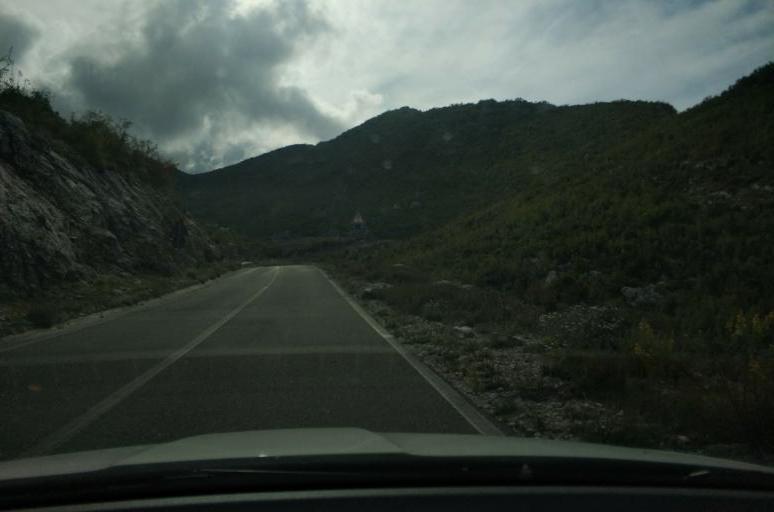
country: AL
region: Durres
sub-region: Rrethi i Krujes
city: Kruje
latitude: 41.5288
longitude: 19.7963
